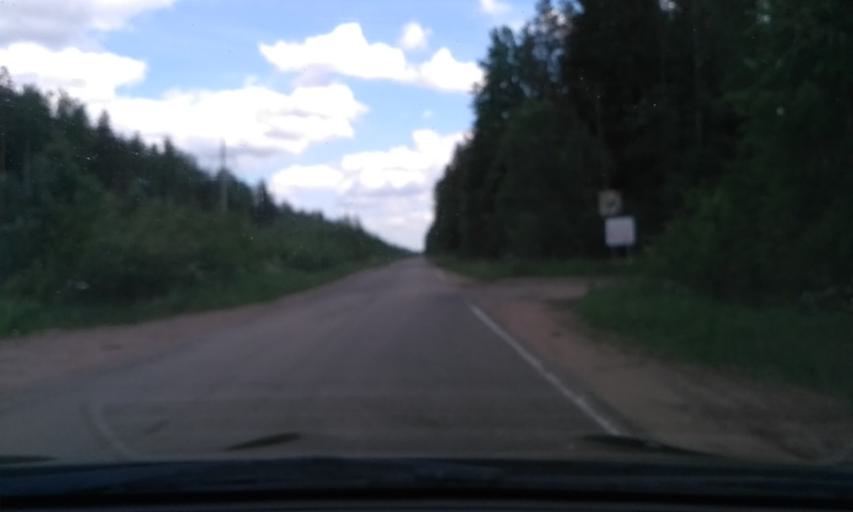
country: RU
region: Leningrad
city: Otradnoye
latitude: 59.8215
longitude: 30.7735
